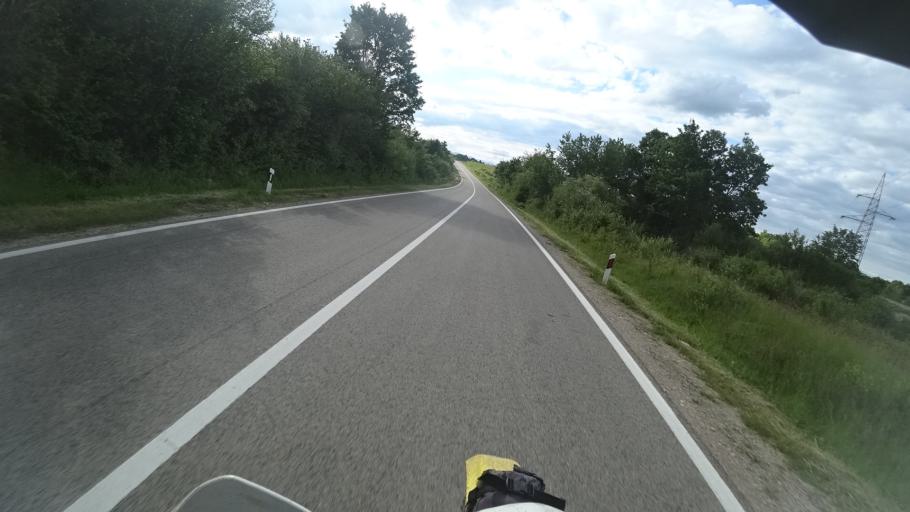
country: HR
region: Licko-Senjska
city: Gospic
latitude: 44.5013
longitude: 15.4518
